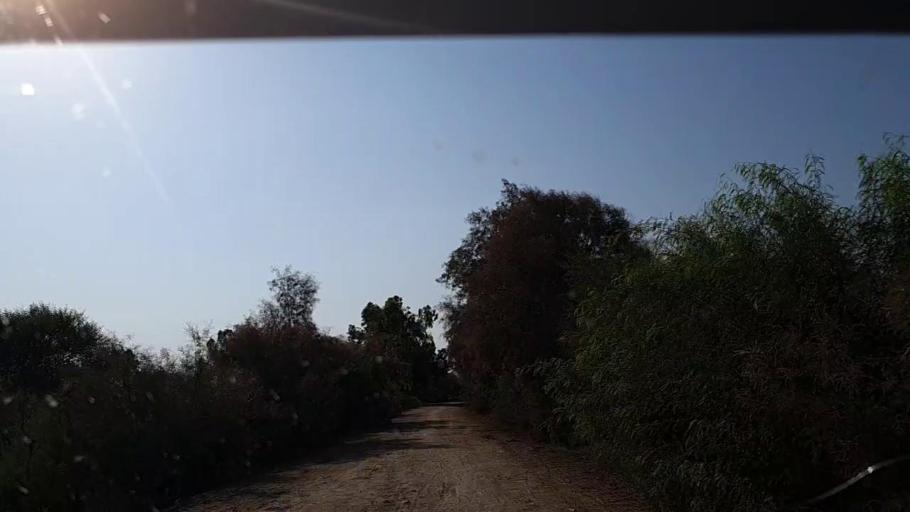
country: PK
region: Sindh
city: Adilpur
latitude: 27.9023
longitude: 69.2291
